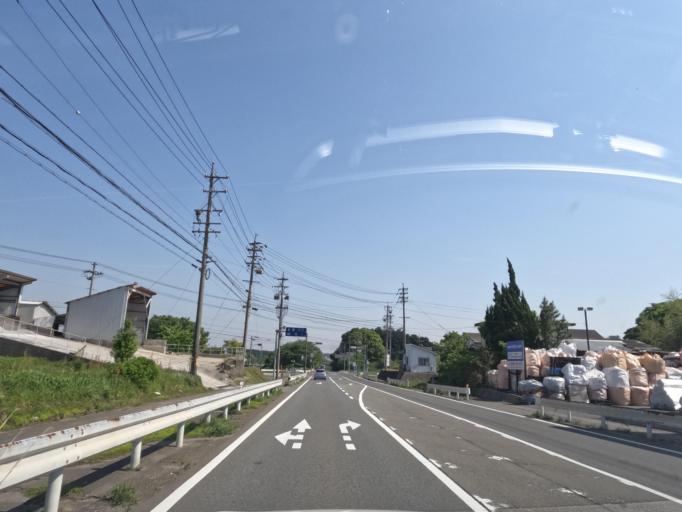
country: JP
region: Mie
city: Komono
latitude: 35.1660
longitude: 136.4996
